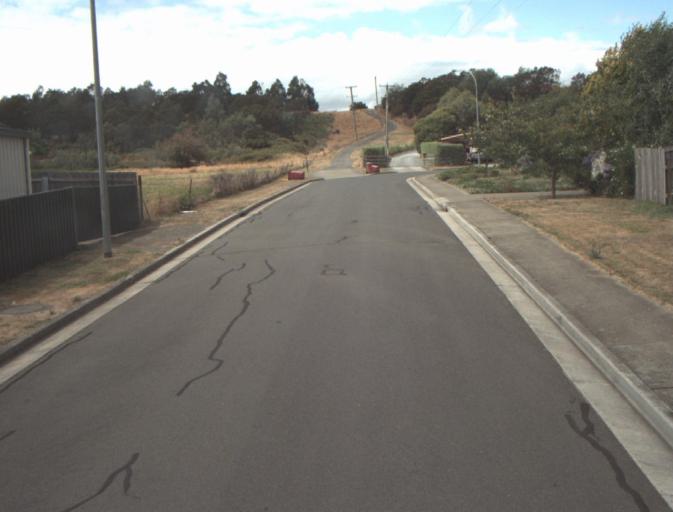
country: AU
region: Tasmania
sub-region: Launceston
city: Newstead
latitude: -41.4494
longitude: 147.1894
